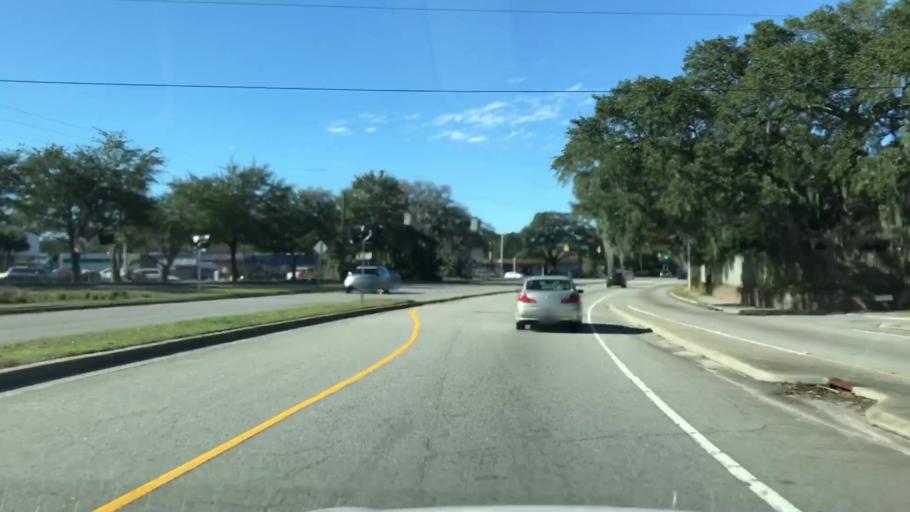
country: US
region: South Carolina
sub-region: Charleston County
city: Charleston
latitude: 32.7808
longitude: -79.9713
